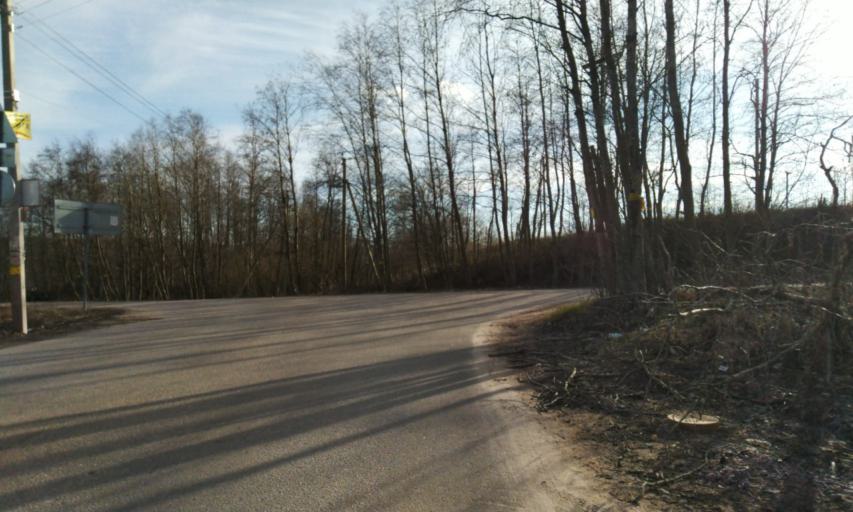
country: RU
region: Leningrad
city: Bugry
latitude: 60.1116
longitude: 30.4229
